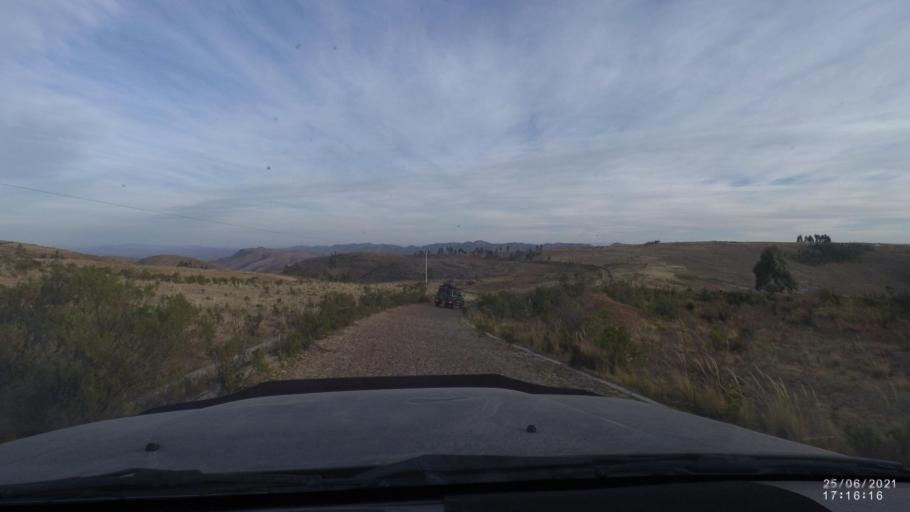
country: BO
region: Cochabamba
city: Arani
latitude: -17.8801
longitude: -65.6996
